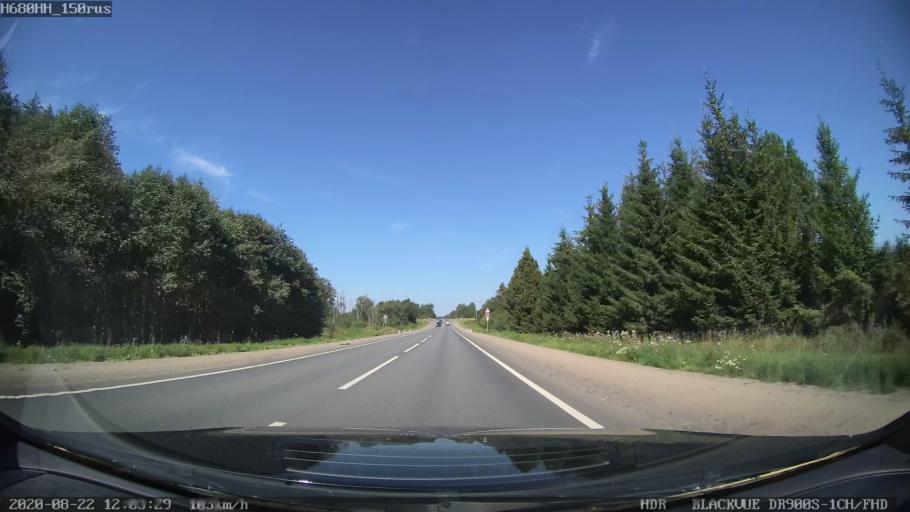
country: RU
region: Tverskaya
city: Rameshki
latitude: 57.2555
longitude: 36.0845
